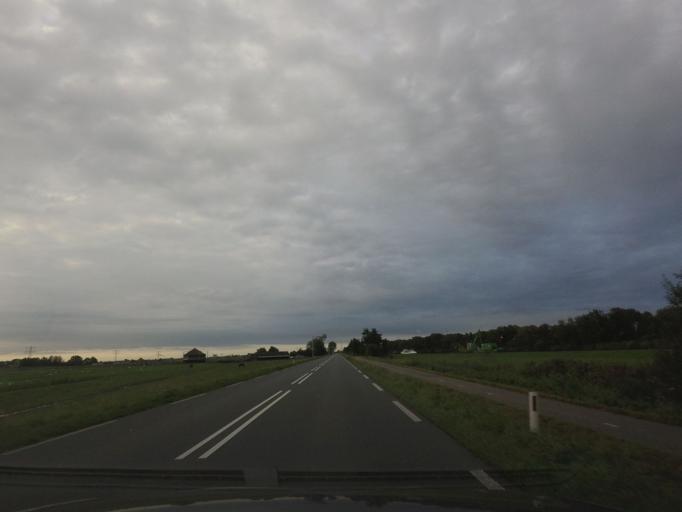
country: NL
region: North Holland
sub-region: Gemeente Uitgeest
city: Uitgeest
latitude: 52.5529
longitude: 4.7803
